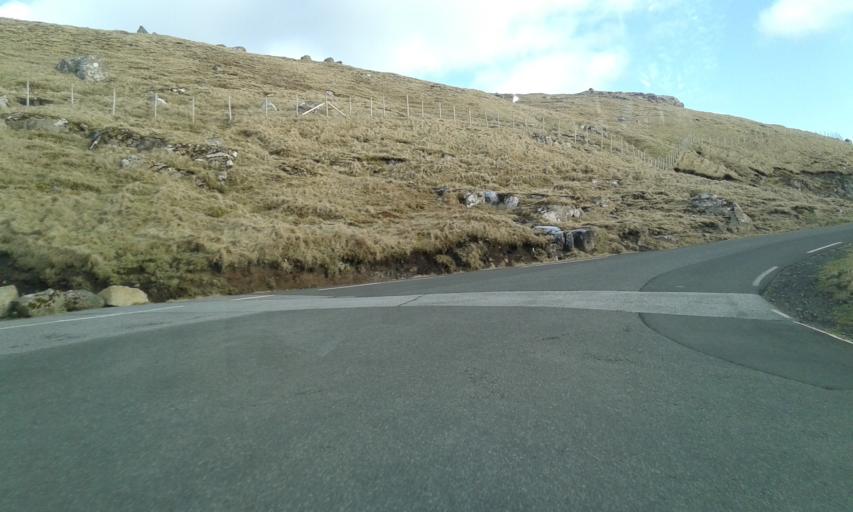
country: FO
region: Streymoy
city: Argir
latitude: 61.9835
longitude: -6.8541
